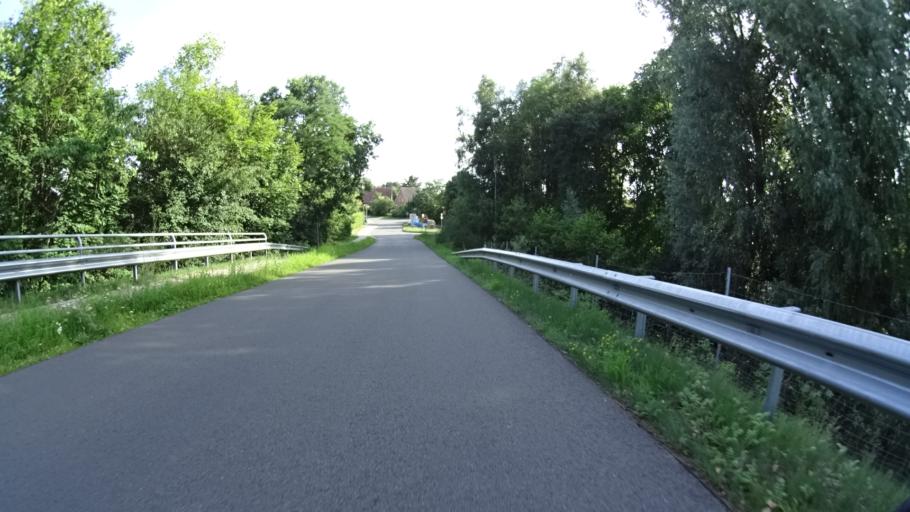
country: DE
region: Lower Saxony
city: Bardowick
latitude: 53.2803
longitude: 10.3901
